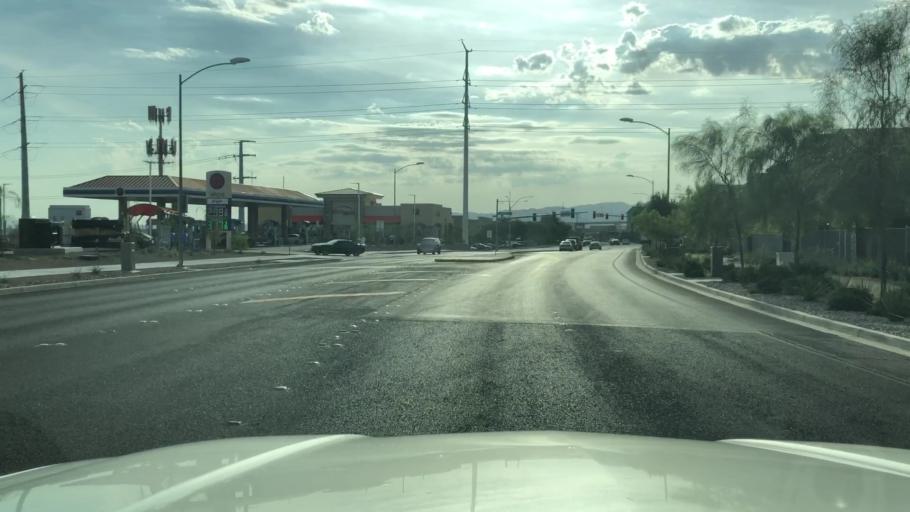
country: US
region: Nevada
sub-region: Clark County
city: Henderson
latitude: 36.0340
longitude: -115.0313
